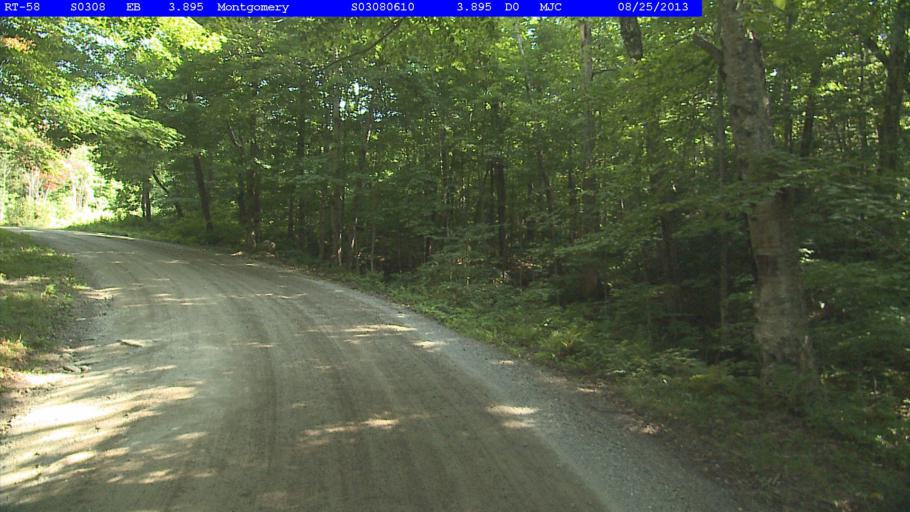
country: US
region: Vermont
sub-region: Franklin County
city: Richford
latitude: 44.8477
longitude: -72.5484
